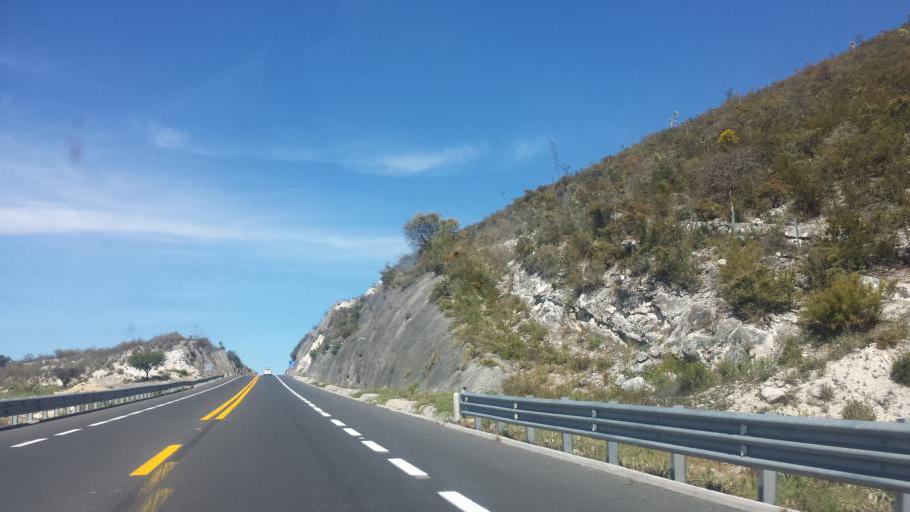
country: MX
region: Puebla
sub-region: San Jose Miahuatlan
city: San Pedro Tetitlan
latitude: 18.0037
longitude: -97.3554
